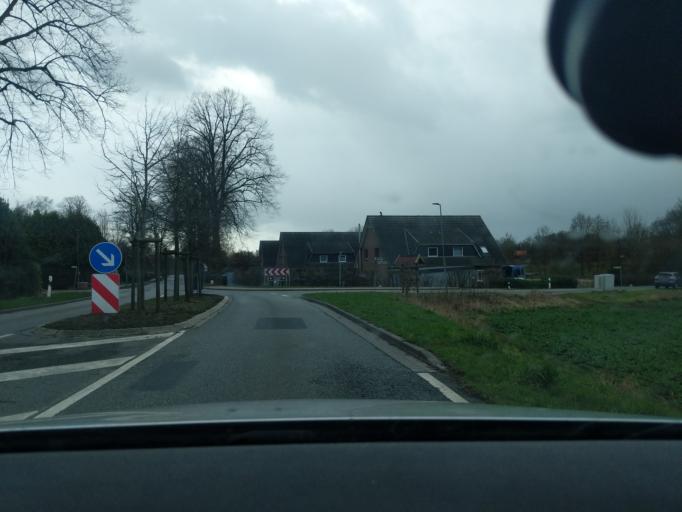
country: DE
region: Lower Saxony
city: Harsefeld
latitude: 53.4887
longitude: 9.5219
